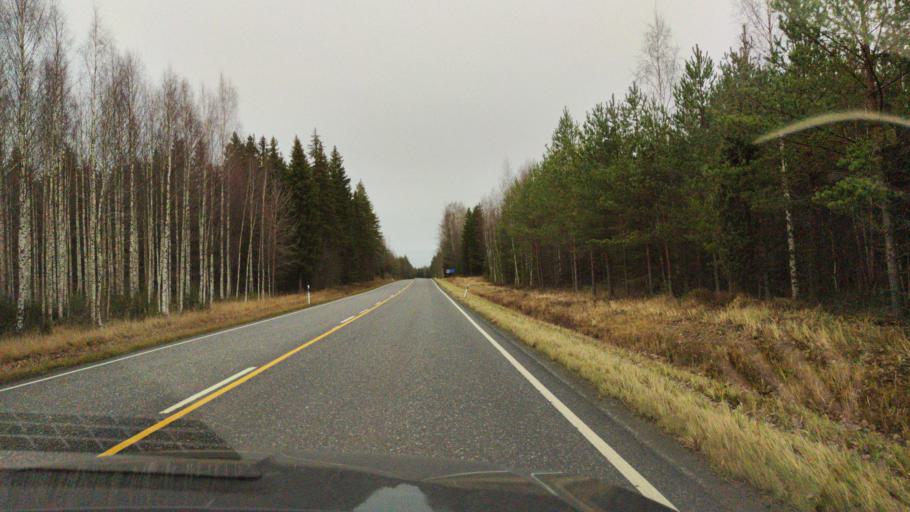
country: FI
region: Varsinais-Suomi
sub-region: Loimaa
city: Aura
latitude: 60.7160
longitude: 22.4446
